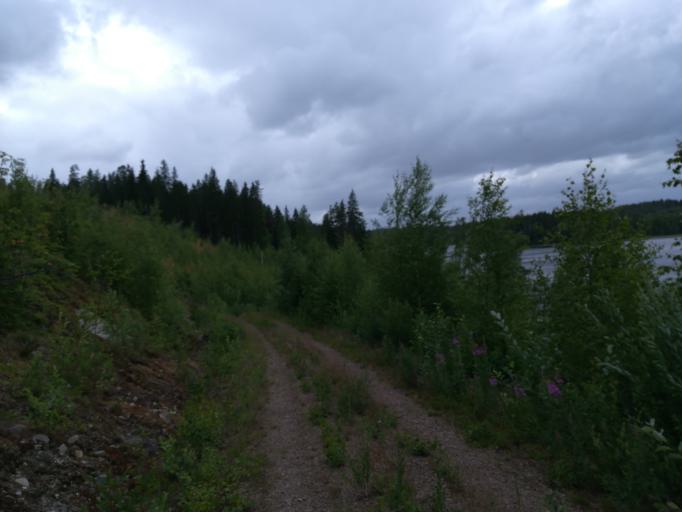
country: FI
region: South Karelia
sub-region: Lappeenranta
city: Savitaipale
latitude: 61.1849
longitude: 27.5558
